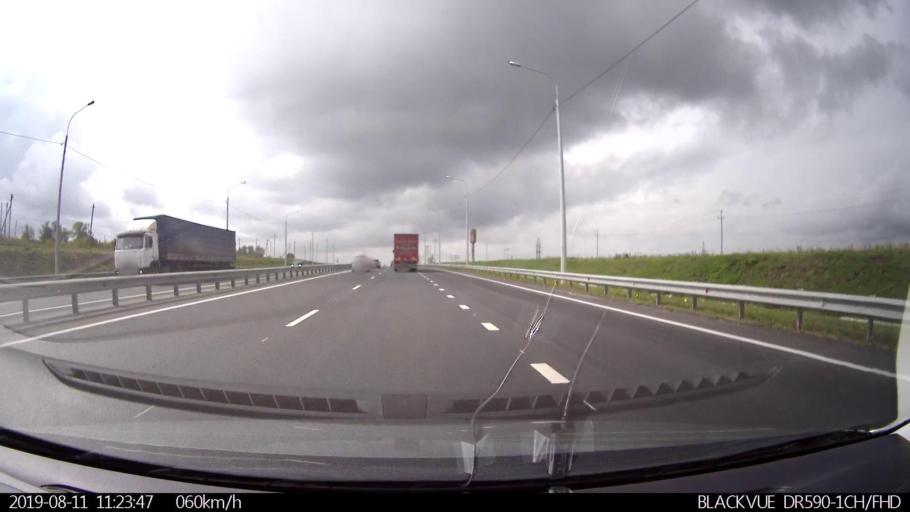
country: RU
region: Ulyanovsk
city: Krasnyy Gulyay
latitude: 54.1328
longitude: 48.2487
